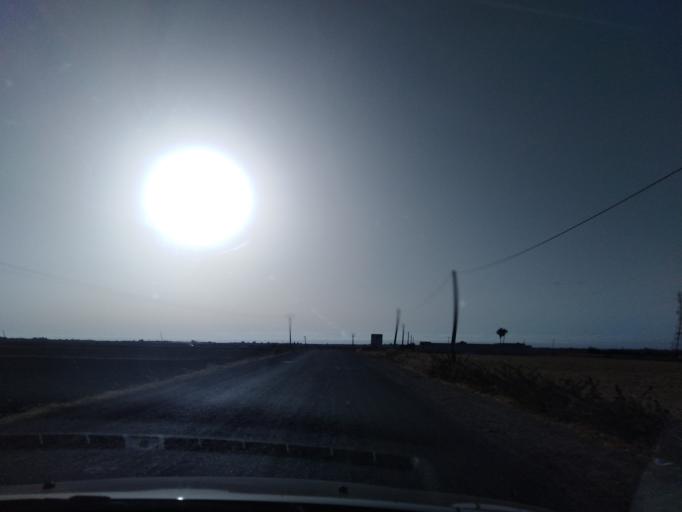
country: MA
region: Doukkala-Abda
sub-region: Safi
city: Safi
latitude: 32.4923
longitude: -8.9271
